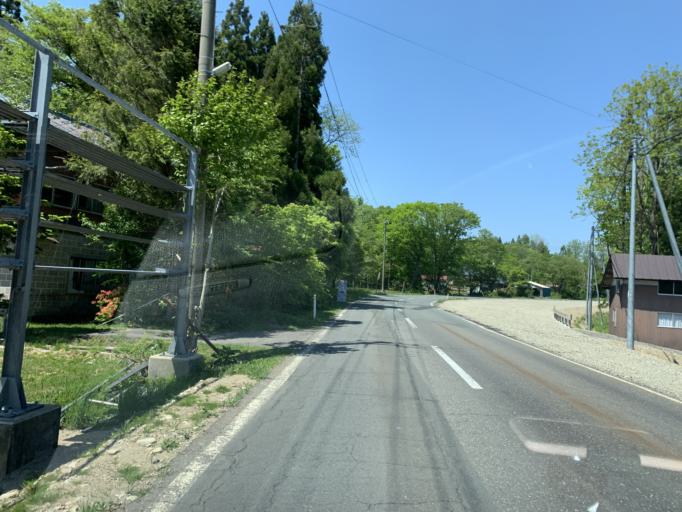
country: JP
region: Iwate
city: Shizukuishi
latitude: 39.5352
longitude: 140.8335
